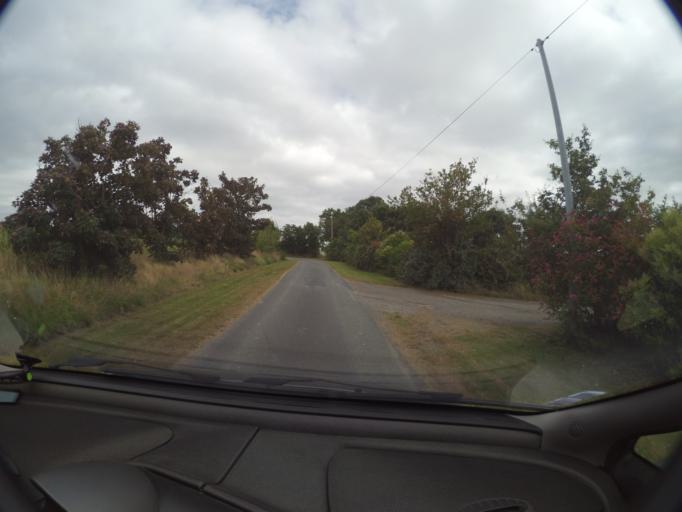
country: FR
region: Pays de la Loire
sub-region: Departement de la Vendee
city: Saint-Hilaire-de-Loulay
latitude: 47.0042
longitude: -1.3521
